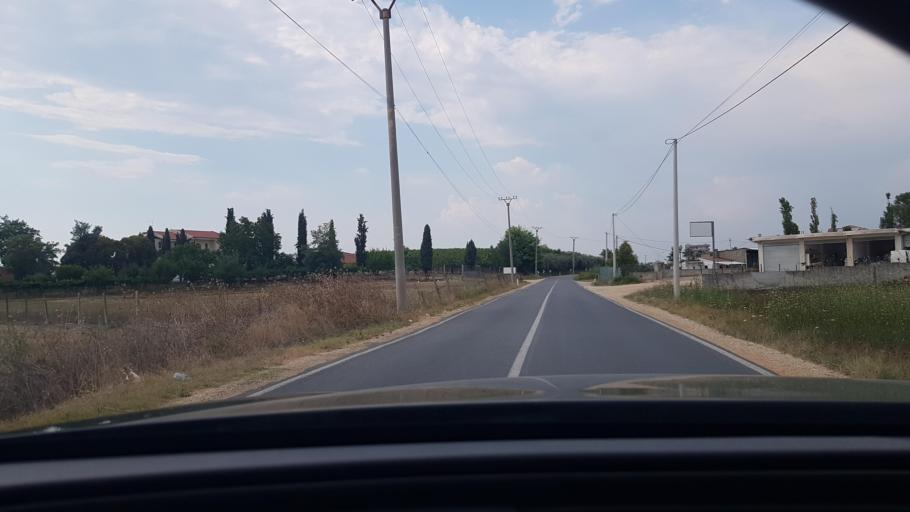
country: AL
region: Durres
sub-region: Rrethi i Durresit
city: Katundi i Ri
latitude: 41.4131
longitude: 19.5466
